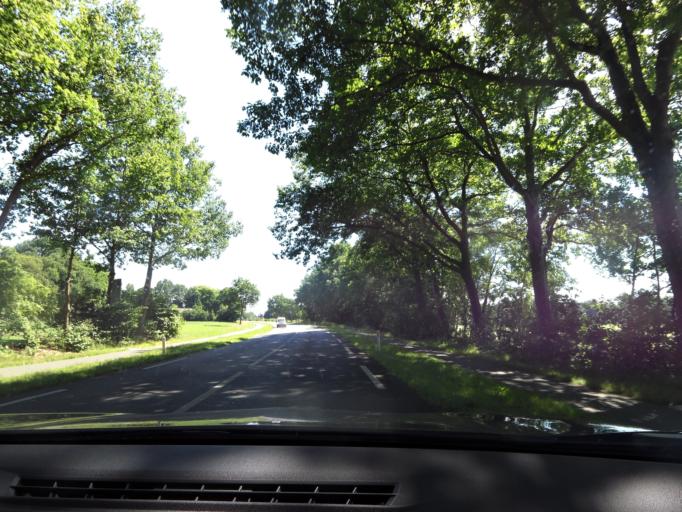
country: NL
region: Gelderland
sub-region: Berkelland
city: Neede
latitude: 52.1525
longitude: 6.6062
